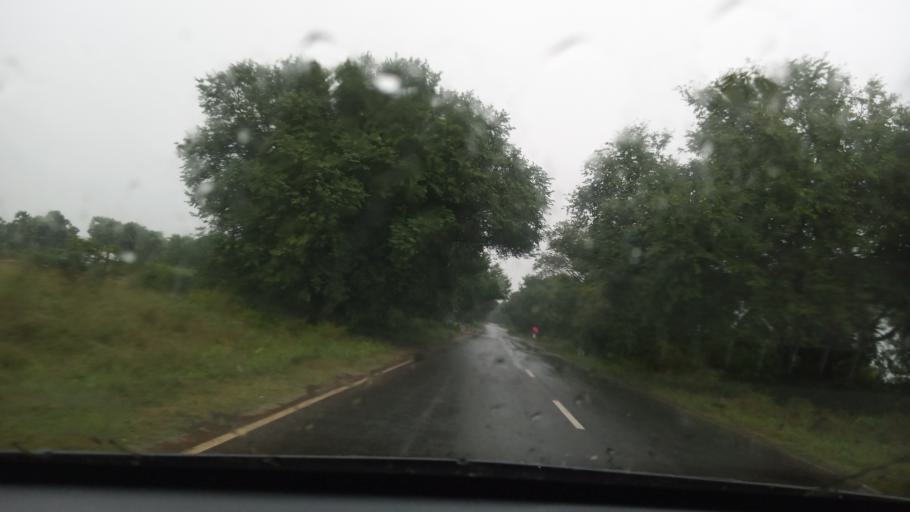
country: IN
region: Tamil Nadu
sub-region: Vellore
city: Kalavai
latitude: 12.8334
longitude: 79.4053
